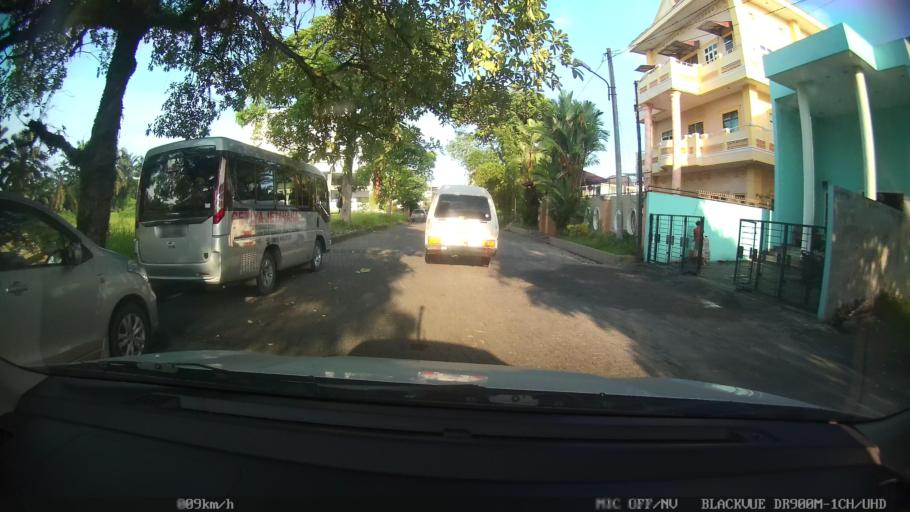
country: ID
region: North Sumatra
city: Medan
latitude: 3.6202
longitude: 98.6539
